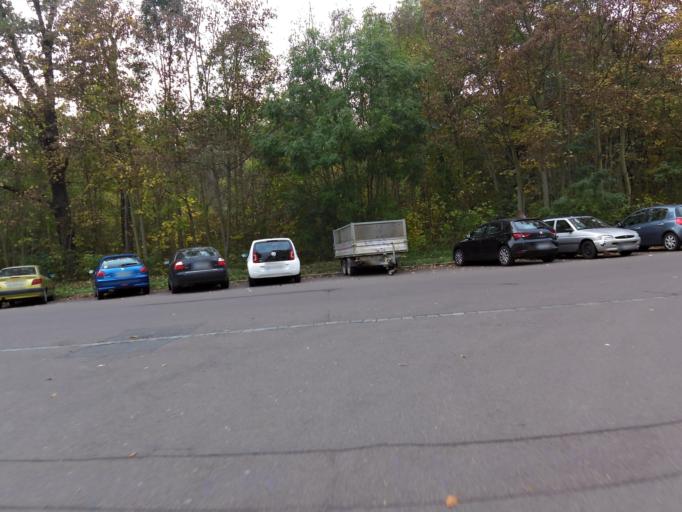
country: DE
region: Saxony
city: Leipzig
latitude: 51.3180
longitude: 12.3658
